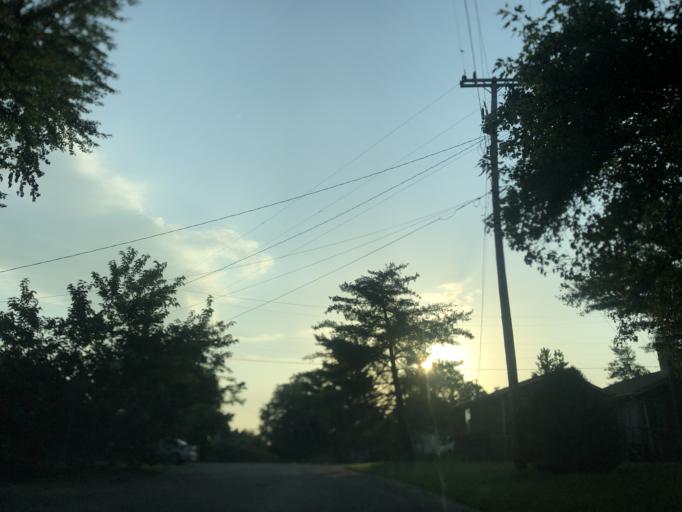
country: US
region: Tennessee
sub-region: Davidson County
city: Lakewood
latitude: 36.1417
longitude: -86.6328
